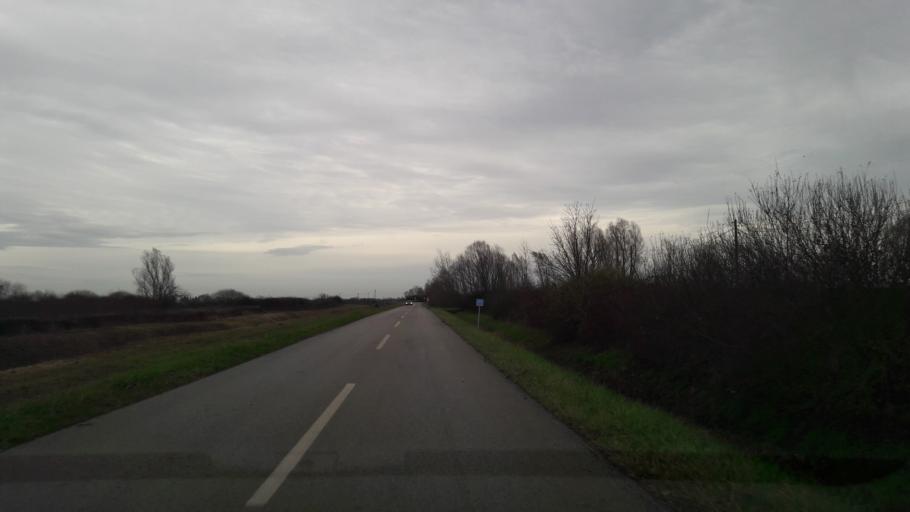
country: HR
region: Osjecko-Baranjska
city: Velimirovac
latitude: 45.6330
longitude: 18.1193
